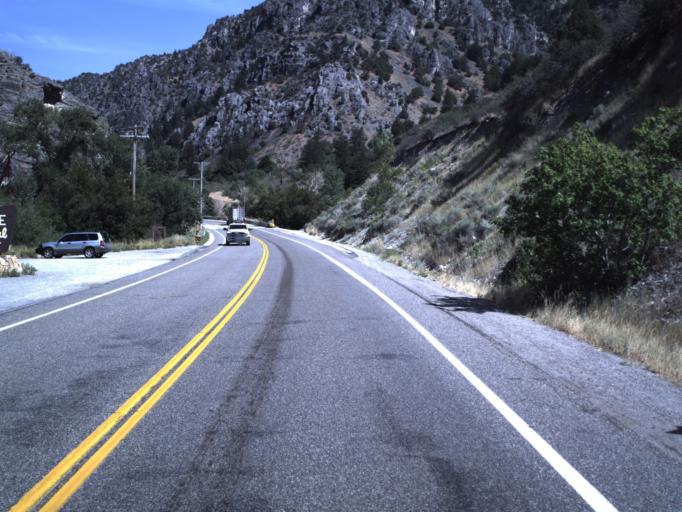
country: US
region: Utah
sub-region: Cache County
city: North Logan
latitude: 41.7419
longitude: -111.7766
